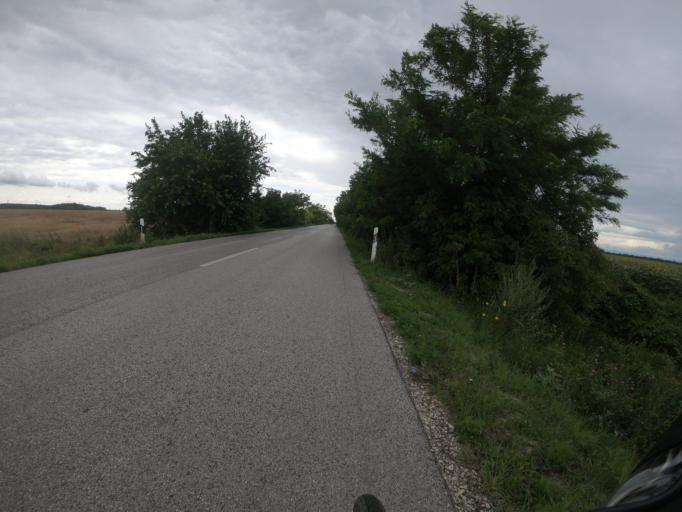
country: HU
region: Heves
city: Poroszlo
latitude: 47.6970
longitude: 20.7232
